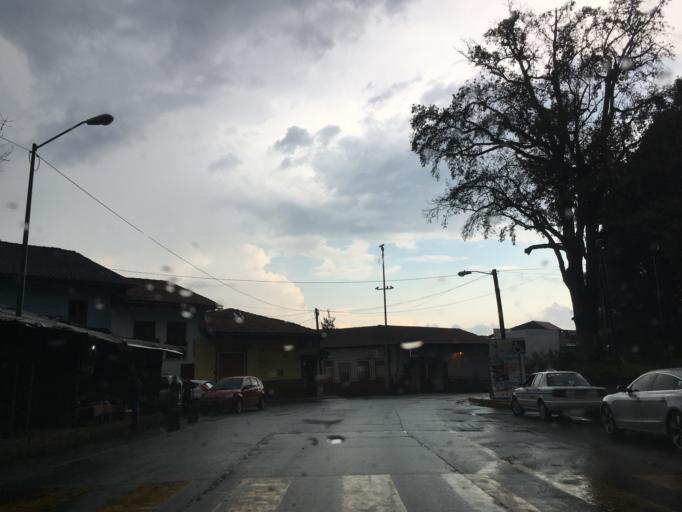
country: MX
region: Michoacan
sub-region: Uruapan
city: Uruapan
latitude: 19.4247
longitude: -102.0712
